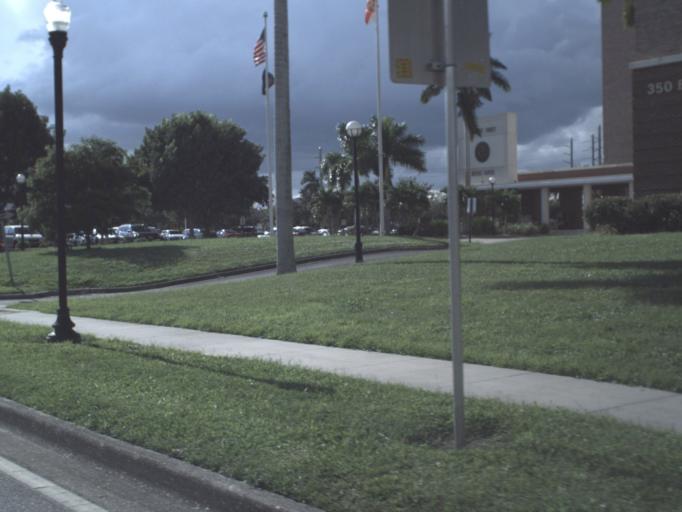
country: US
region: Florida
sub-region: Charlotte County
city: Punta Gorda
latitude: 26.9379
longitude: -82.0469
